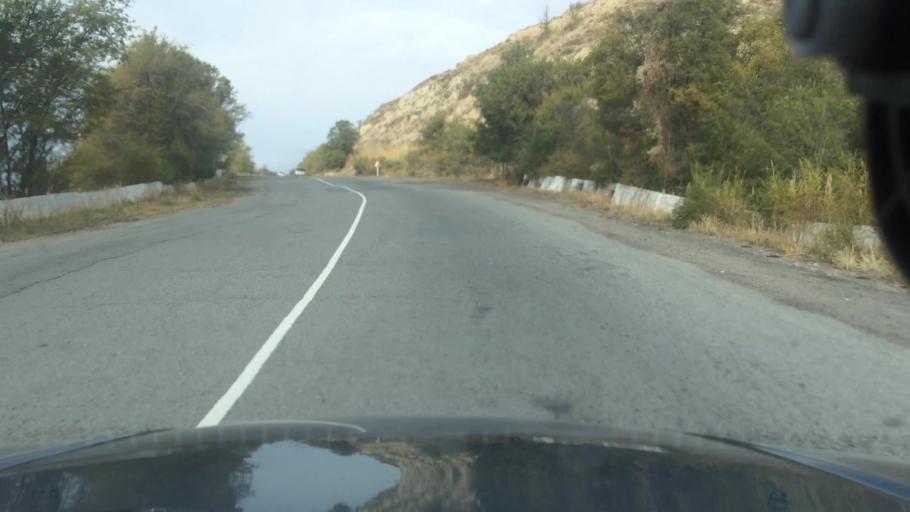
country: KG
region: Ysyk-Koel
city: Karakol
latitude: 42.5951
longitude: 78.3836
